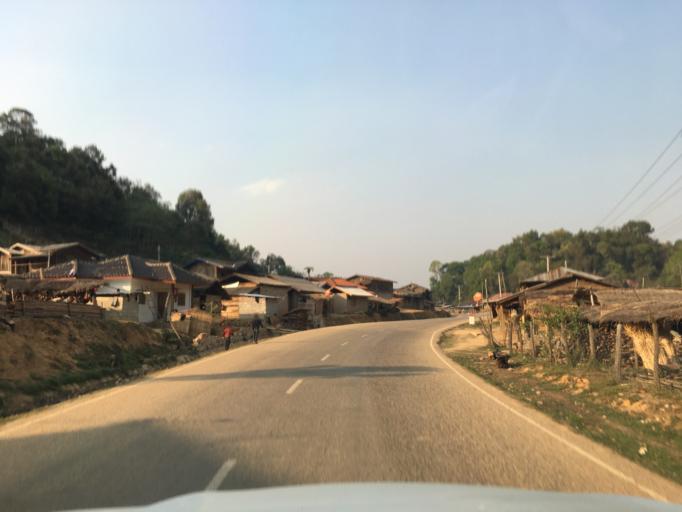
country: LA
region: Houaphan
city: Xam Nua
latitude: 20.5940
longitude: 104.0674
